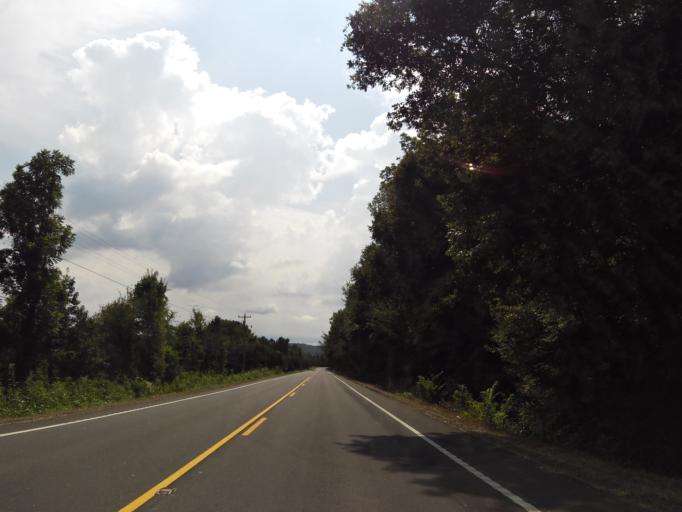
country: US
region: Tennessee
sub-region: Perry County
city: Linden
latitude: 35.7241
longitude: -87.7996
